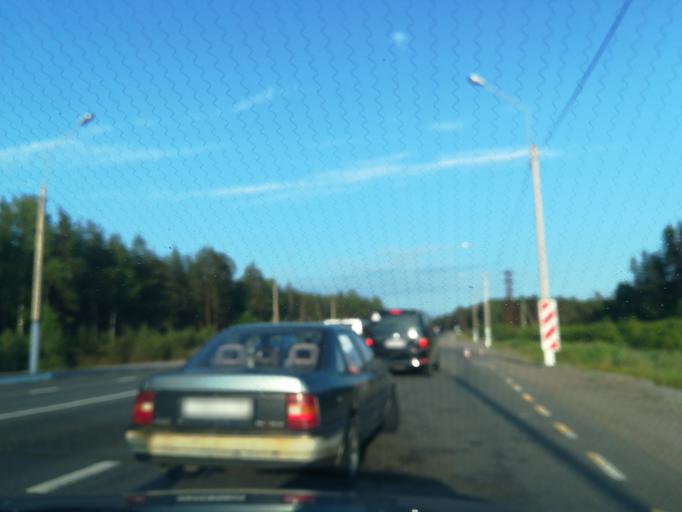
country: RU
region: Leningrad
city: Vyborg
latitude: 60.6640
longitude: 28.9311
